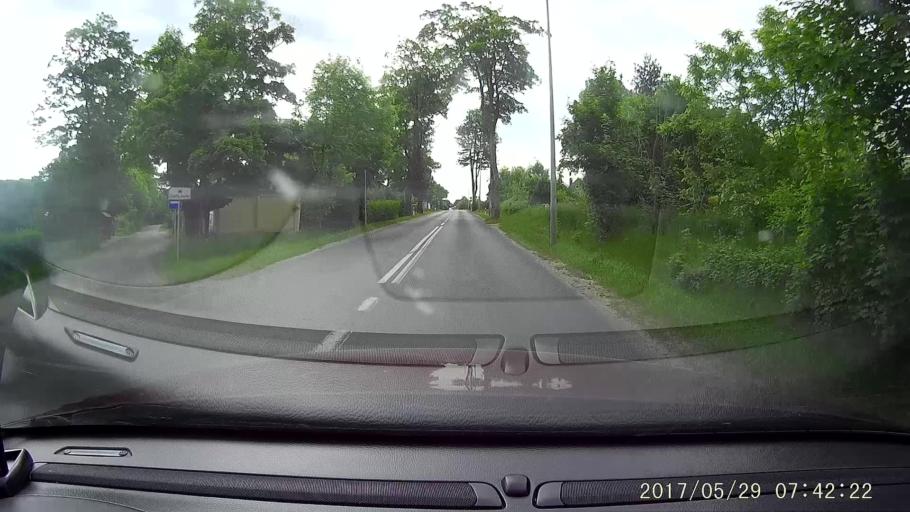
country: PL
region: Lower Silesian Voivodeship
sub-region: Powiat boleslawiecki
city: Boleslawiec
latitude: 51.2526
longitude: 15.5863
